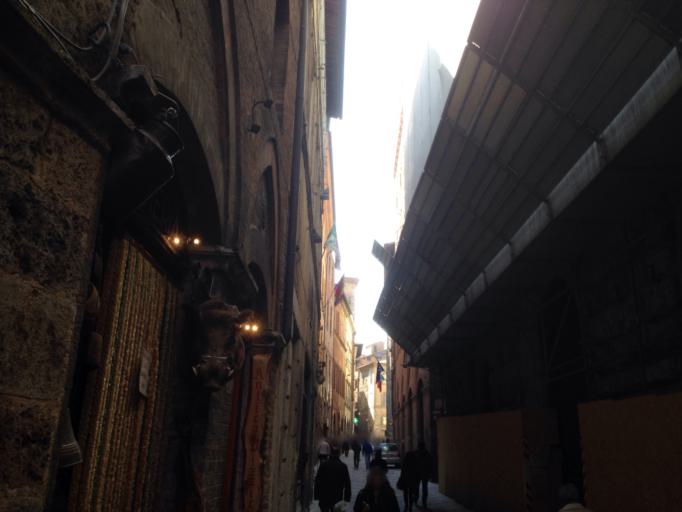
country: IT
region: Tuscany
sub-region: Provincia di Siena
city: Siena
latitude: 43.3171
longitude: 11.3308
